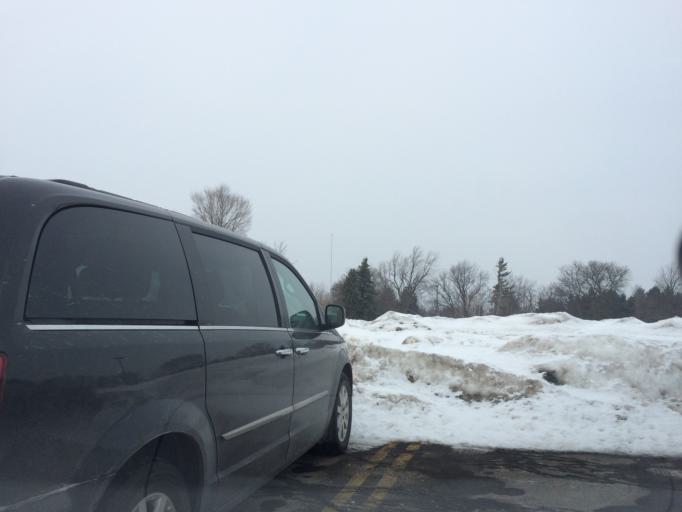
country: US
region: New York
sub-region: Monroe County
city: Fairport
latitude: 43.0841
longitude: -77.4308
